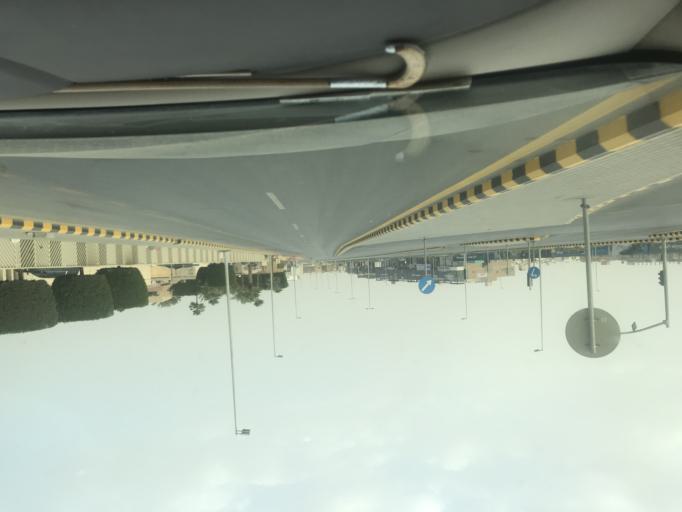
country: SA
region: Ar Riyad
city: Riyadh
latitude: 24.8016
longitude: 46.6538
